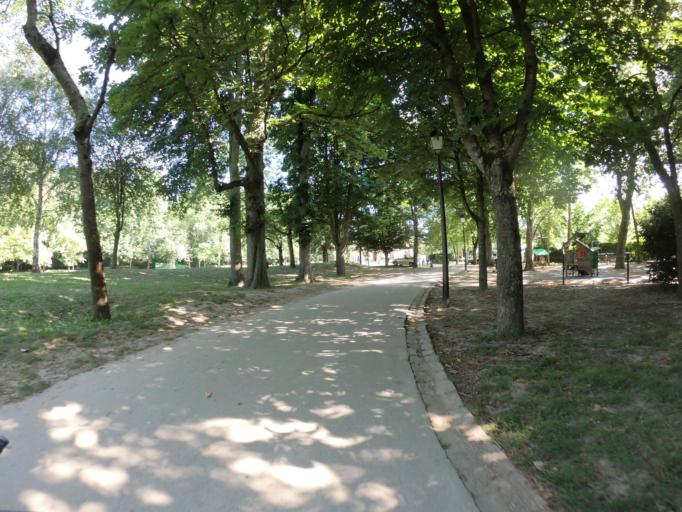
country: FR
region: Ile-de-France
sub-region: Departement des Hauts-de-Seine
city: Antony
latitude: 48.7472
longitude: 2.2933
